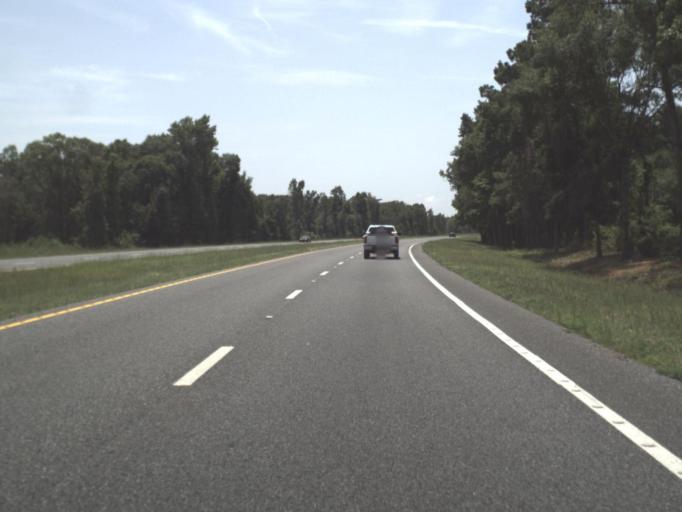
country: US
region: Florida
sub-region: Taylor County
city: Perry
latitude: 29.9455
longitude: -83.4516
